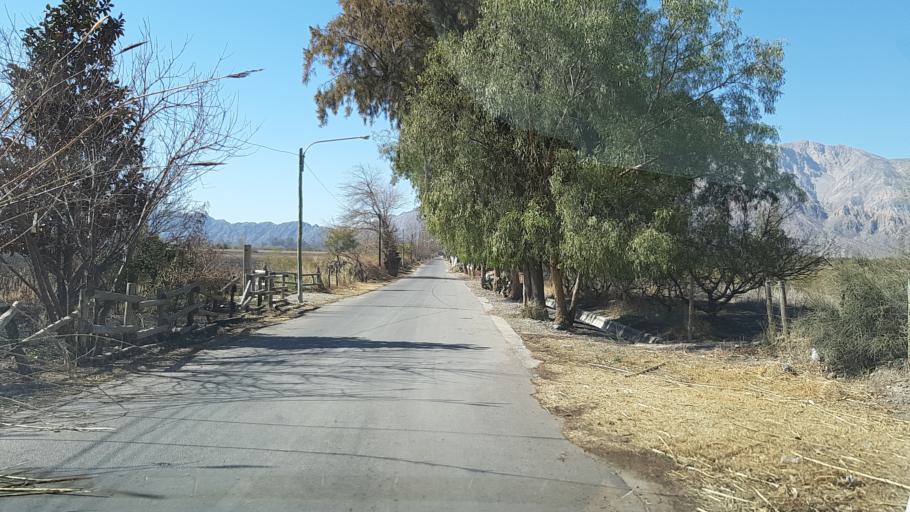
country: AR
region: San Juan
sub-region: Departamento de Zonda
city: Zonda
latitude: -31.5716
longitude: -68.7562
